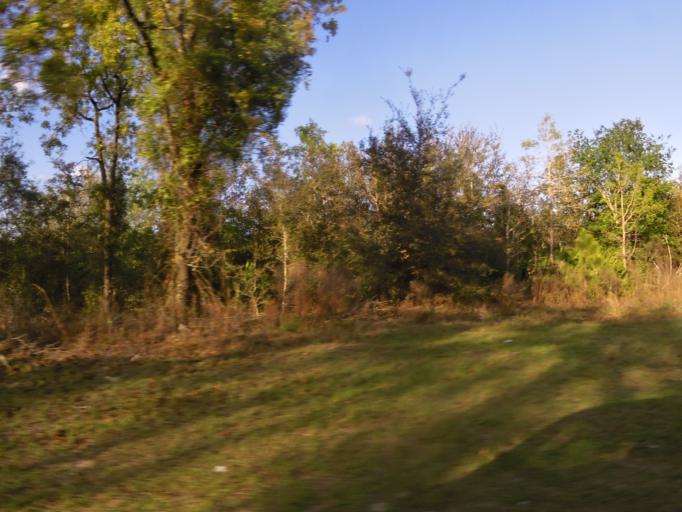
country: US
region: Florida
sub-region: Saint Johns County
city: Fruit Cove
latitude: 30.0753
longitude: -81.5186
